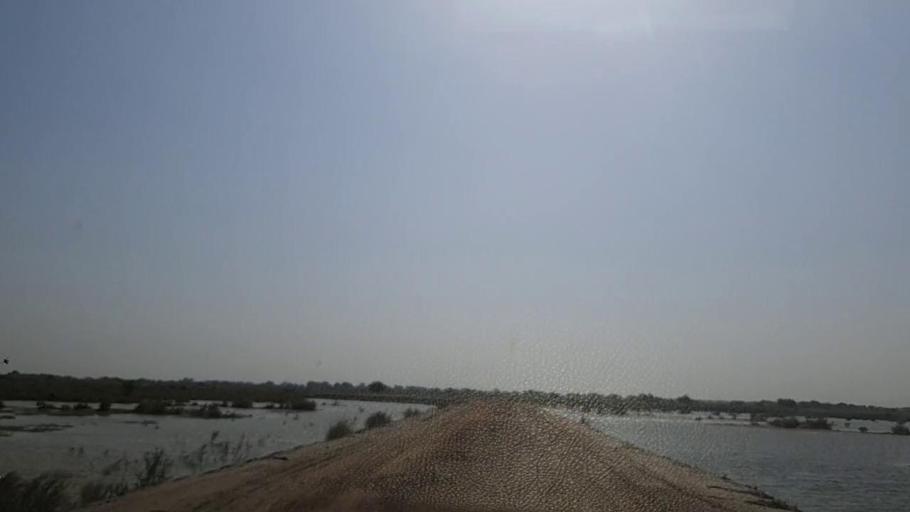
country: PK
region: Sindh
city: Daro Mehar
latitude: 24.7048
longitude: 68.1272
